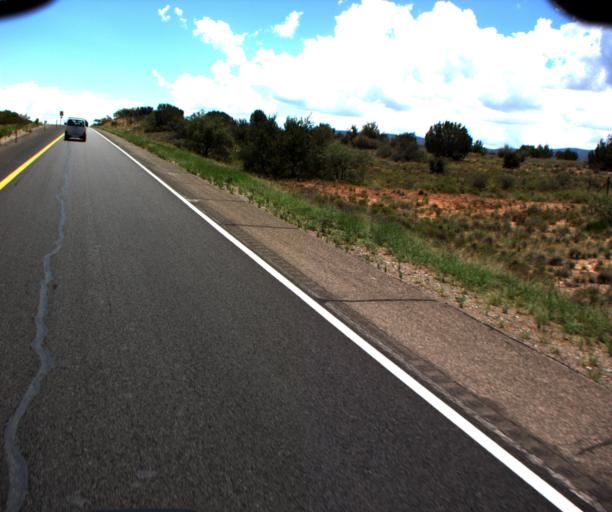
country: US
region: Arizona
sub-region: Yavapai County
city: Verde Village
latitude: 34.6642
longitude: -111.9676
